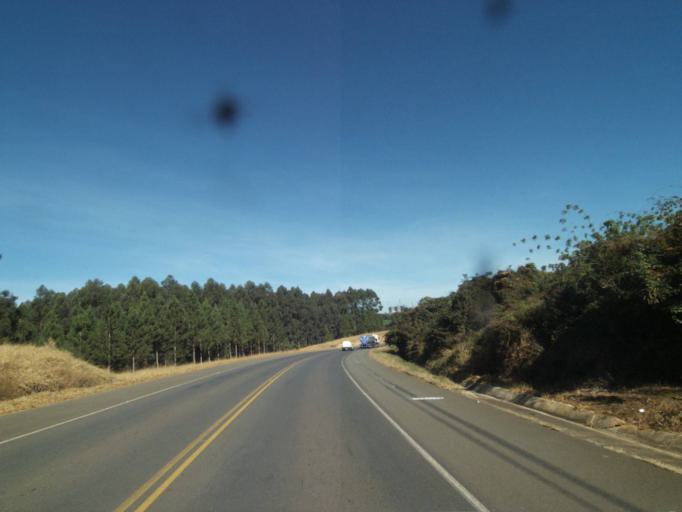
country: BR
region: Parana
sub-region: Tibagi
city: Tibagi
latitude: -24.5165
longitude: -50.4361
